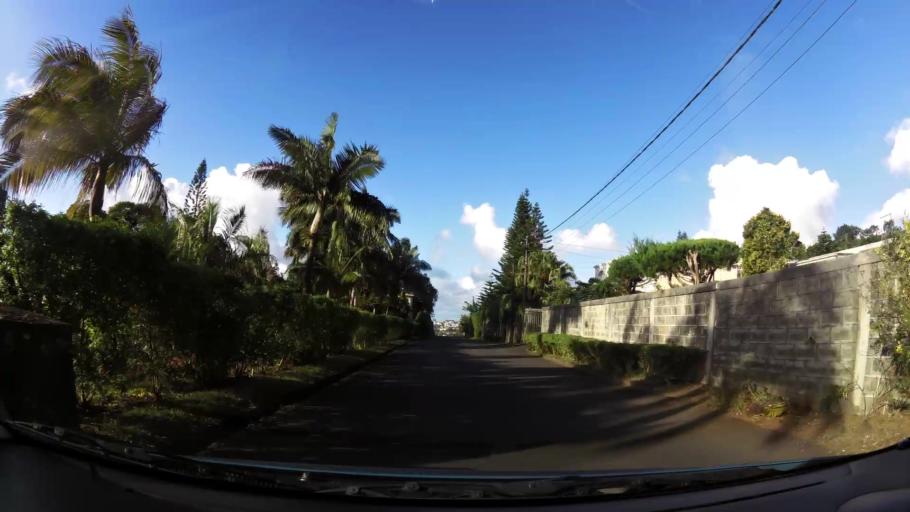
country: MU
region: Plaines Wilhems
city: Curepipe
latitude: -20.3161
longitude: 57.5104
